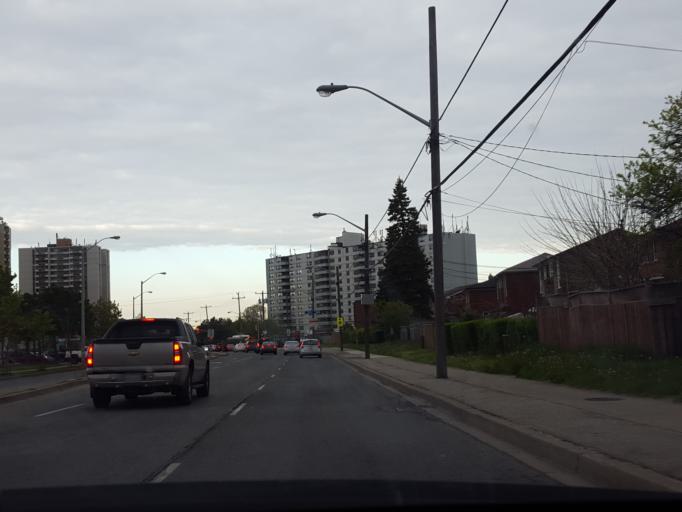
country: CA
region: Ontario
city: Toronto
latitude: 43.7096
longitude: -79.4755
